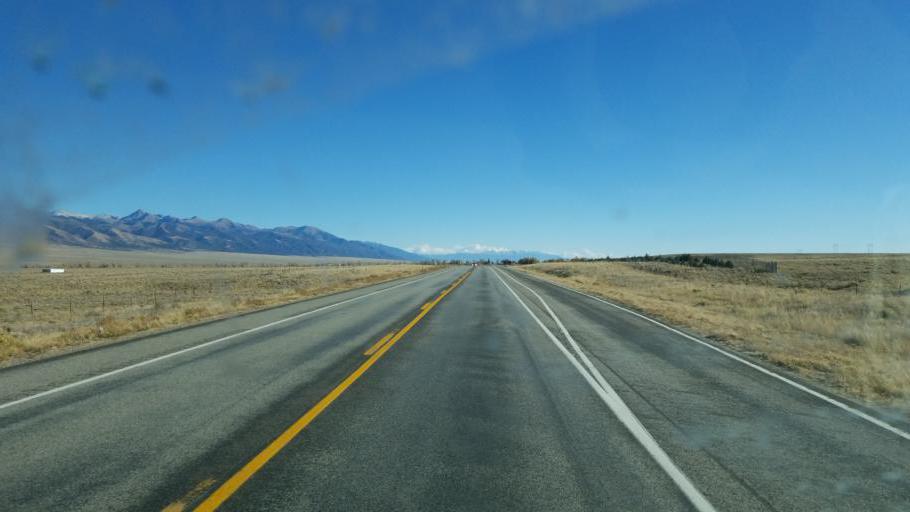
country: US
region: Colorado
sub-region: Saguache County
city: Saguache
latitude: 38.2619
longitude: -105.9592
